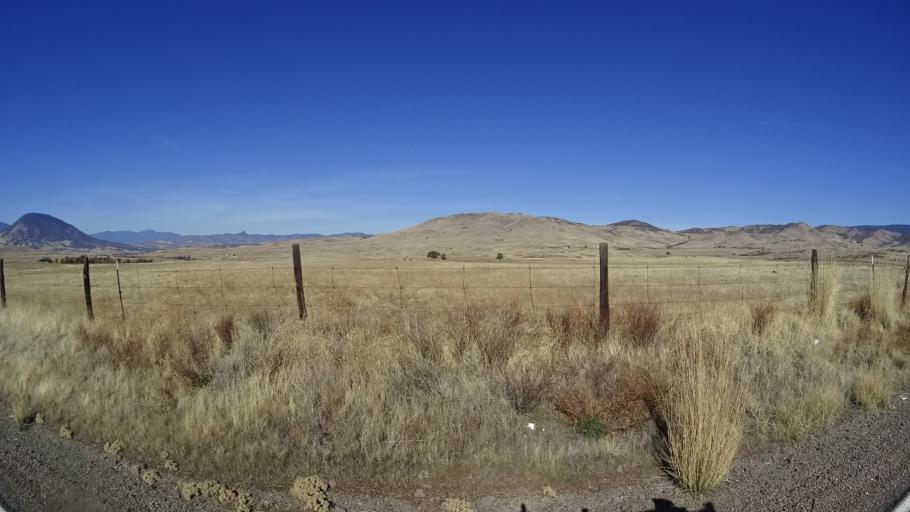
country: US
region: California
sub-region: Siskiyou County
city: Montague
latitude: 41.8045
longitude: -122.4031
